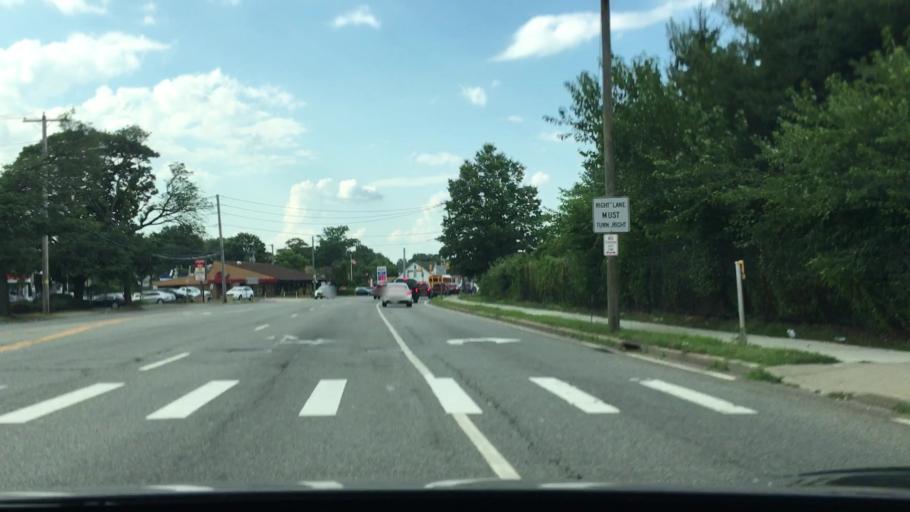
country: US
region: New York
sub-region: Nassau County
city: Westbury
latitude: 40.7461
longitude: -73.5871
